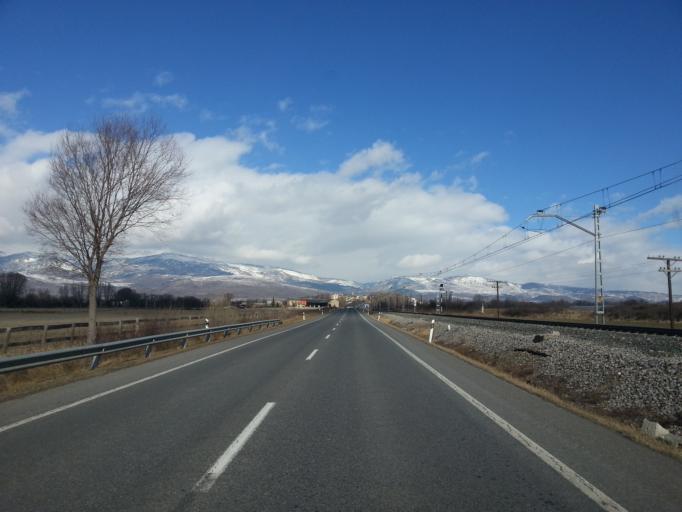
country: ES
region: Catalonia
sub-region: Provincia de Girona
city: Puigcerda
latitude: 42.4090
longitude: 1.9173
